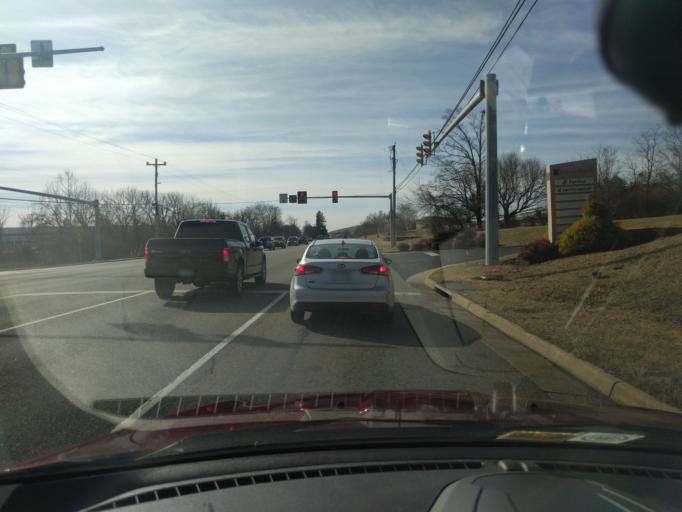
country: US
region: Virginia
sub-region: Augusta County
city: Verona
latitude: 38.1874
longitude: -79.0257
